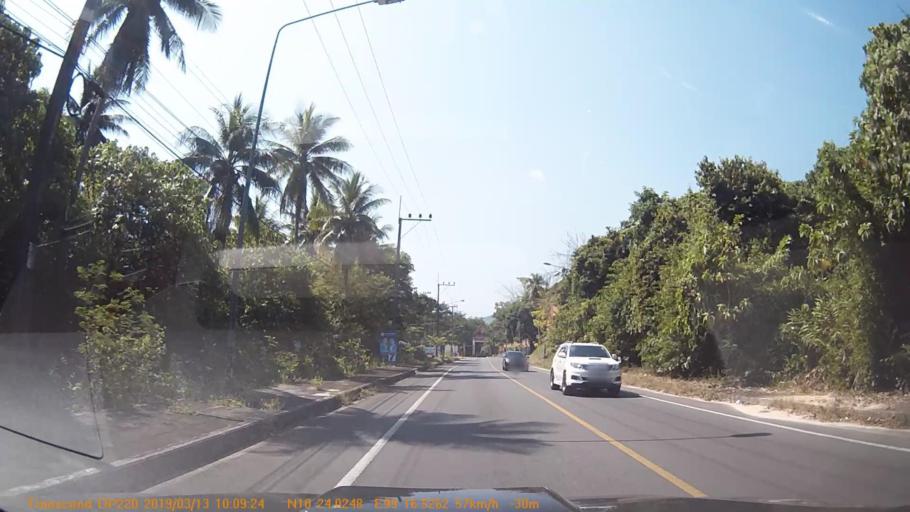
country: TH
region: Chumphon
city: Chumphon
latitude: 10.4006
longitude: 99.2754
